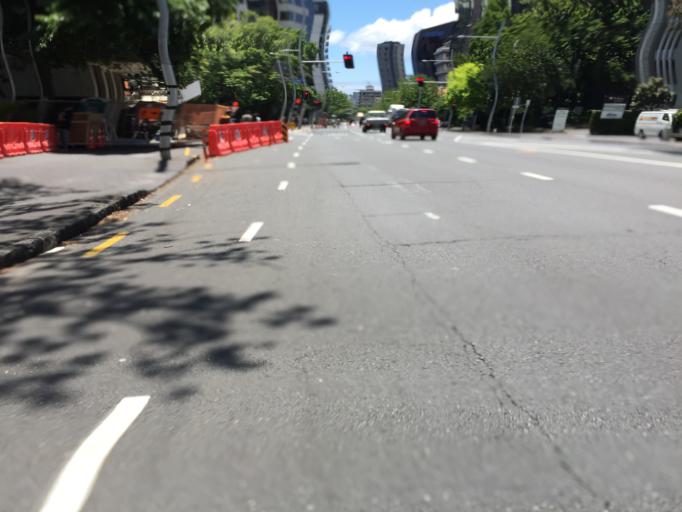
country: NZ
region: Auckland
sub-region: Auckland
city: Auckland
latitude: -36.8567
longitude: 174.7653
